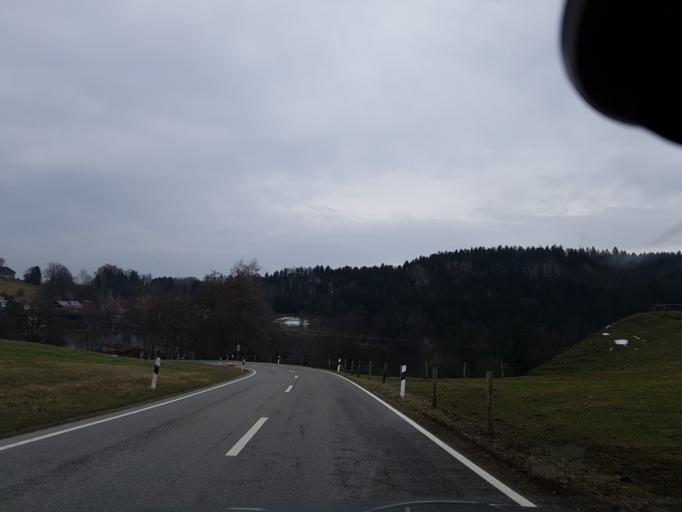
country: DE
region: Bavaria
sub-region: Upper Bavaria
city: Feldkirchen-Westerham
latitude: 47.9404
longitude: 11.8564
